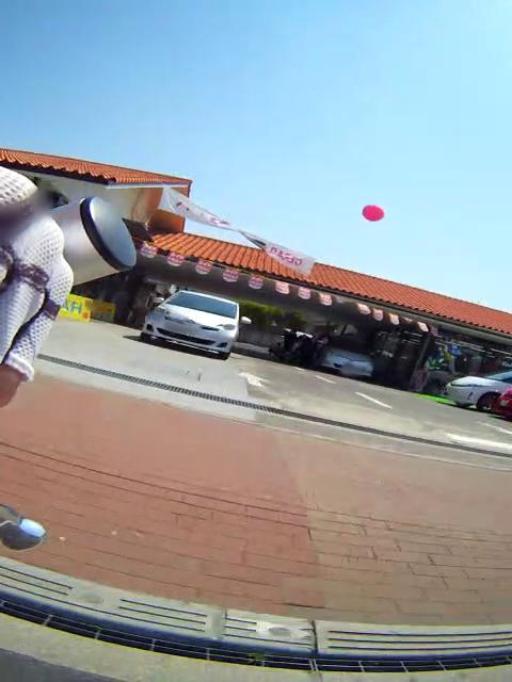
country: JP
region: Osaka
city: Matsubara
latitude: 34.5807
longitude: 135.5510
